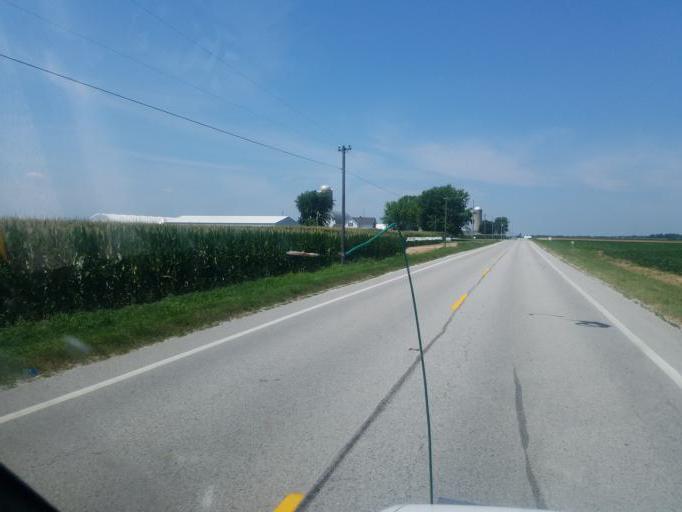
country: US
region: Ohio
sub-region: Auglaize County
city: New Bremen
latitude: 40.4553
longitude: -84.4341
